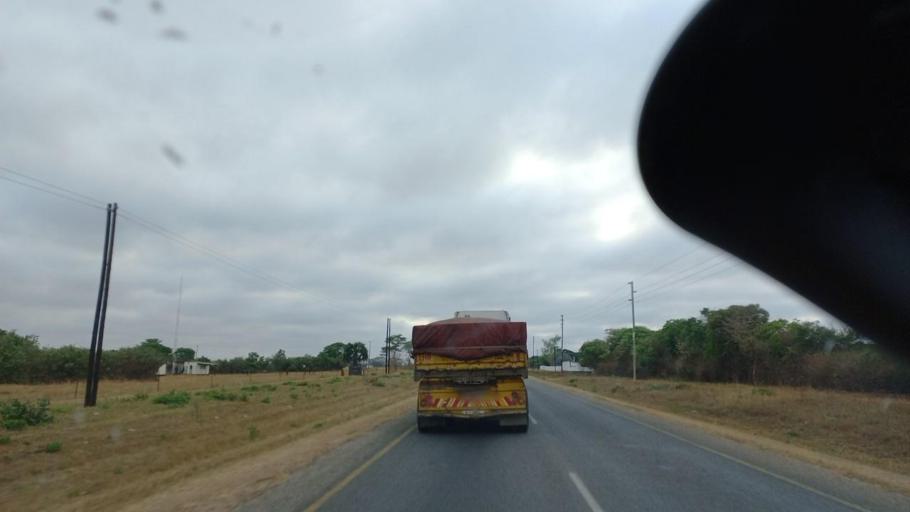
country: ZM
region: Lusaka
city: Chongwe
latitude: -15.3510
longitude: 28.5594
